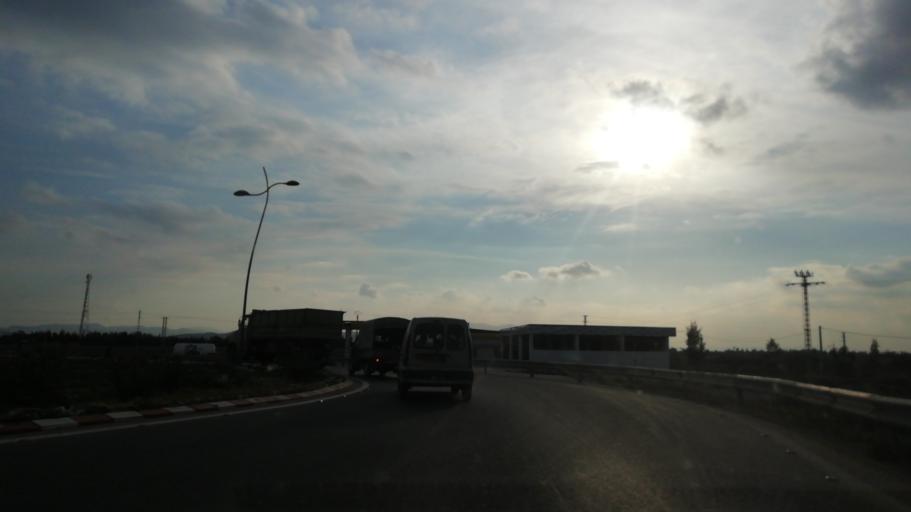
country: DZ
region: Mascara
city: Mascara
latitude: 35.6289
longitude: 0.0613
